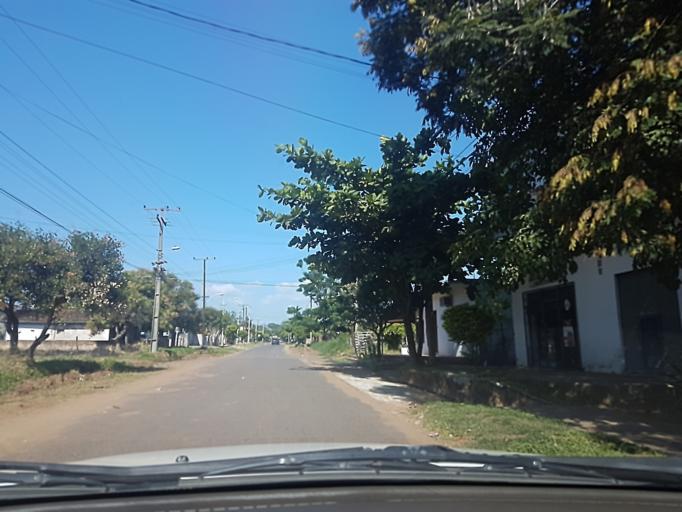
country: PY
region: Central
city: Limpio
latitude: -25.1746
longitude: -57.4781
